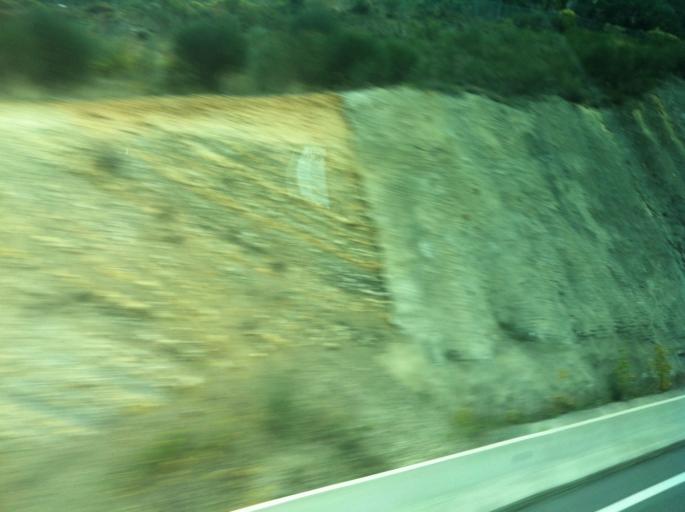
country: ES
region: Basque Country
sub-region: Provincia de Alava
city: Arminon
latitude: 42.7884
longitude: -2.8230
